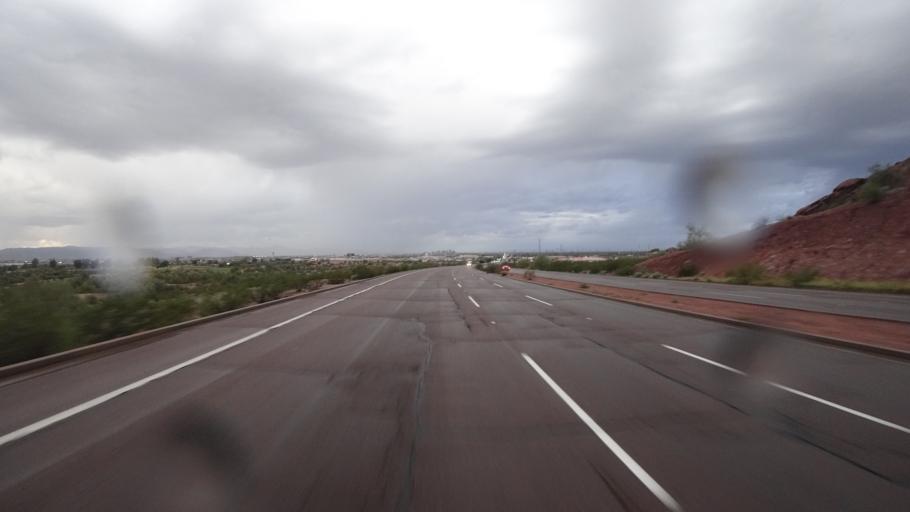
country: US
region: Arizona
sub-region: Maricopa County
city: Tempe Junction
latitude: 33.4656
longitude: -111.9552
